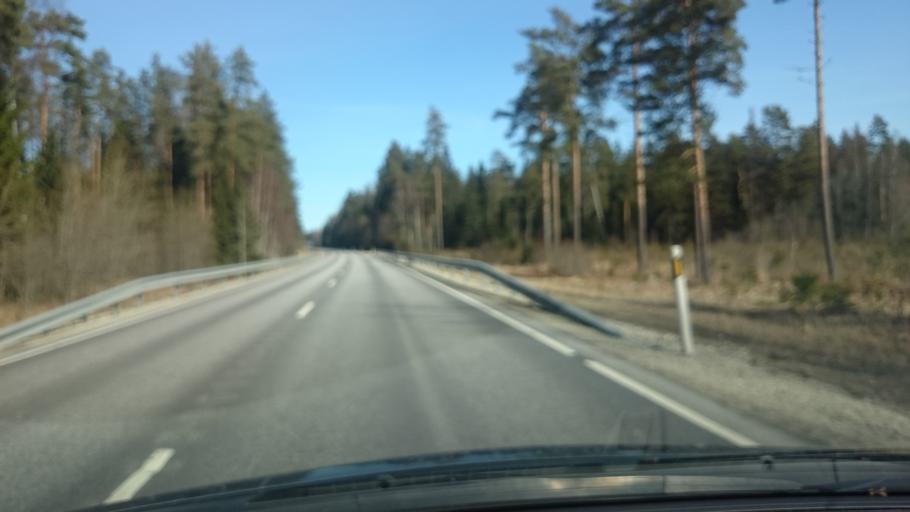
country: EE
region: Paernumaa
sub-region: Vaendra vald (alev)
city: Vandra
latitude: 58.6787
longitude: 25.2275
